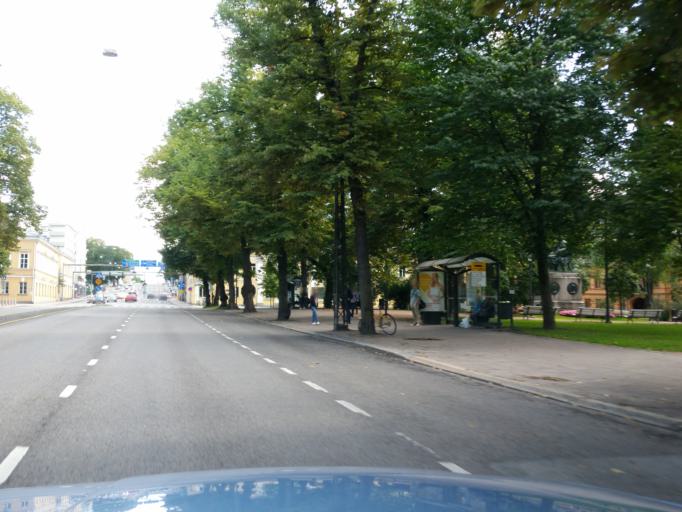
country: FI
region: Varsinais-Suomi
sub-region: Turku
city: Turku
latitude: 60.4518
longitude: 22.2756
